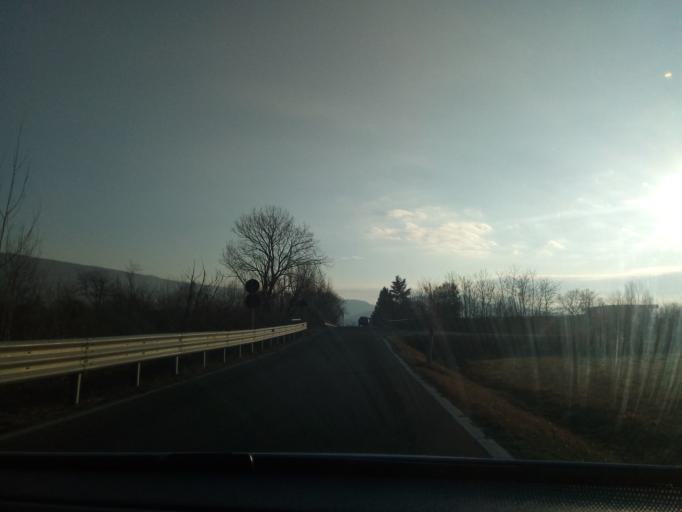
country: IT
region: Piedmont
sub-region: Provincia di Torino
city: Quassolo
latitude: 45.5079
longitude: 7.8376
